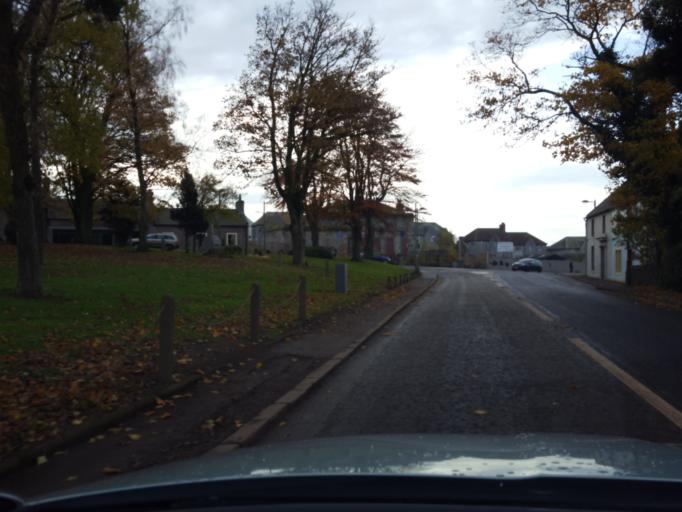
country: GB
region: Scotland
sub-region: South Lanarkshire
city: Carnwath
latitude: 55.7018
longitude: -3.6200
